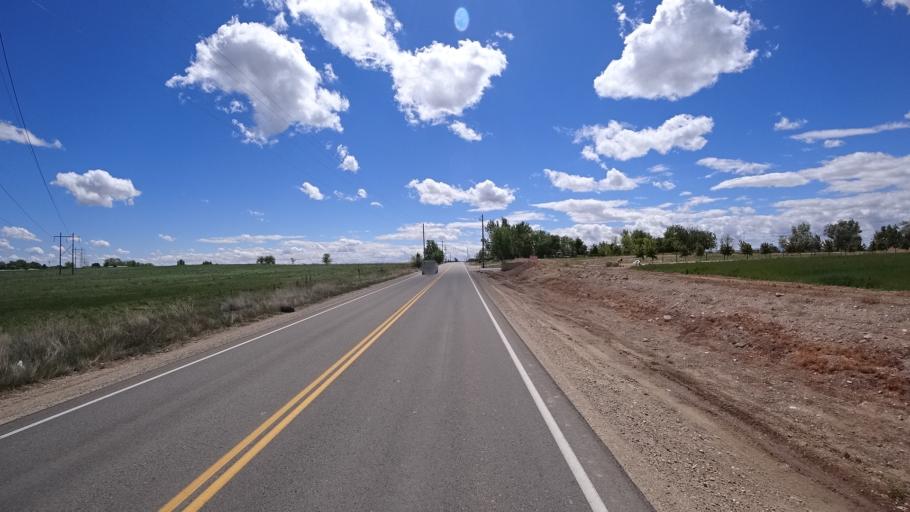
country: US
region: Idaho
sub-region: Ada County
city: Meridian
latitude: 43.5702
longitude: -116.4537
